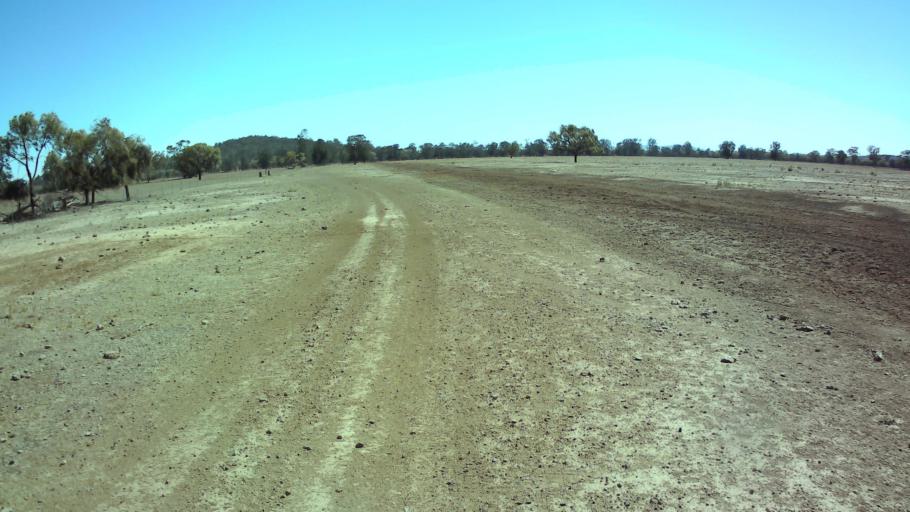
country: AU
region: New South Wales
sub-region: Bland
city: West Wyalong
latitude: -33.7475
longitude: 147.6606
